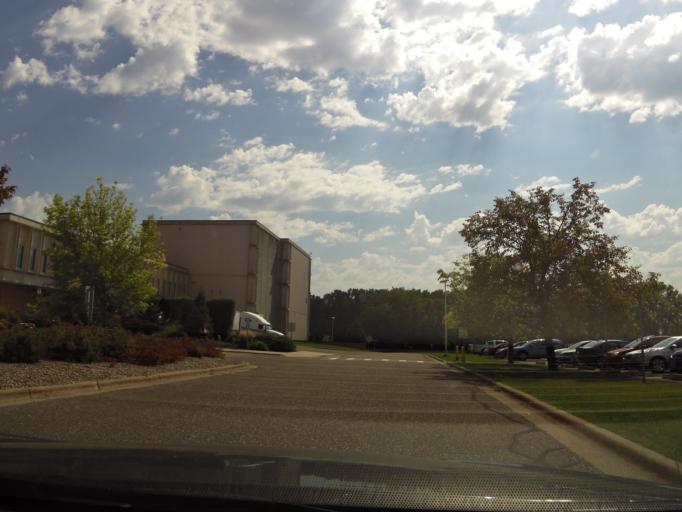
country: US
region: Minnesota
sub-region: Ramsey County
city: Maplewood
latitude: 44.9542
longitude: -92.9872
